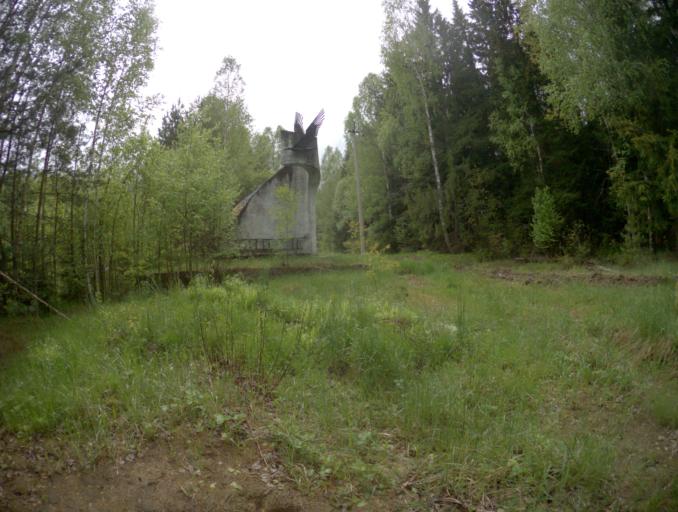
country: RU
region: Vladimir
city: Zolotkovo
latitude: 55.2819
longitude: 41.0434
